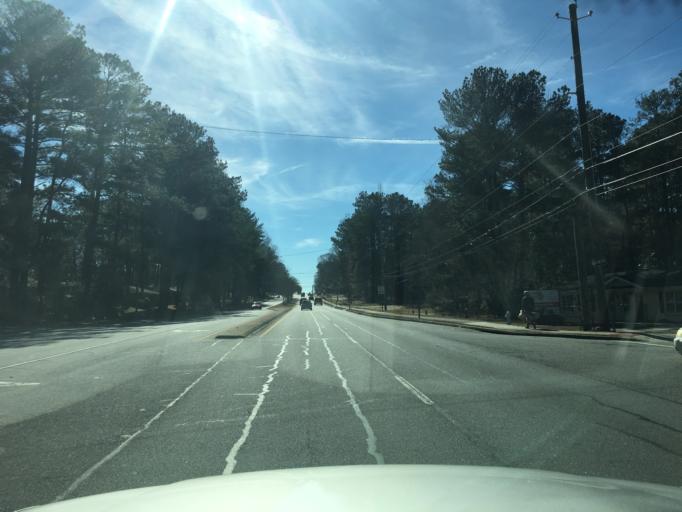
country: US
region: Georgia
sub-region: Gwinnett County
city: Lawrenceville
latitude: 33.9354
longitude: -83.9944
